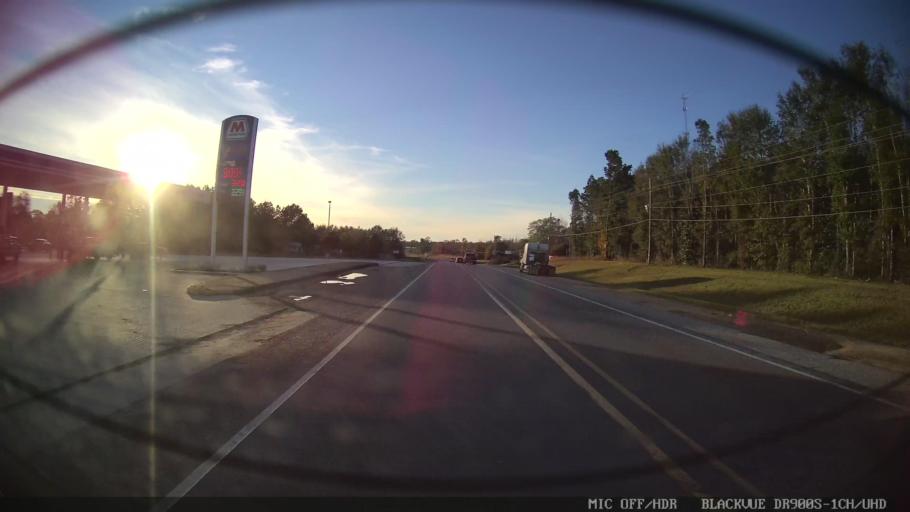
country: US
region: Mississippi
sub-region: Lamar County
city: Lumberton
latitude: 31.0014
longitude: -89.4217
